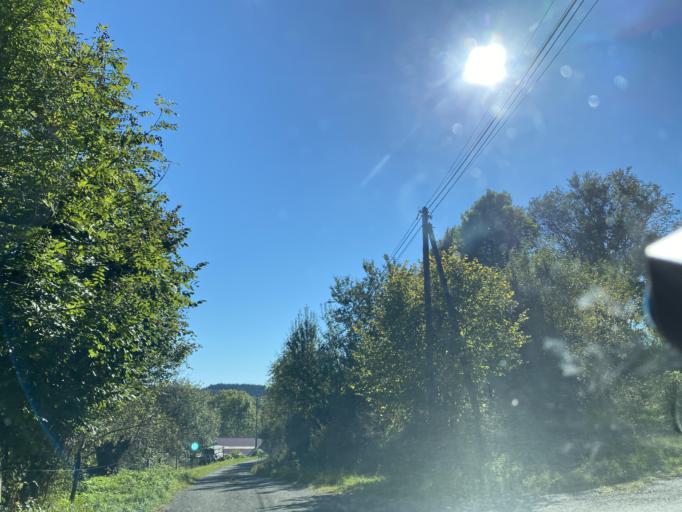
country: FR
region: Rhone-Alpes
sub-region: Departement de la Loire
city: Saint-Just-en-Chevalet
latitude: 45.9570
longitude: 3.8618
